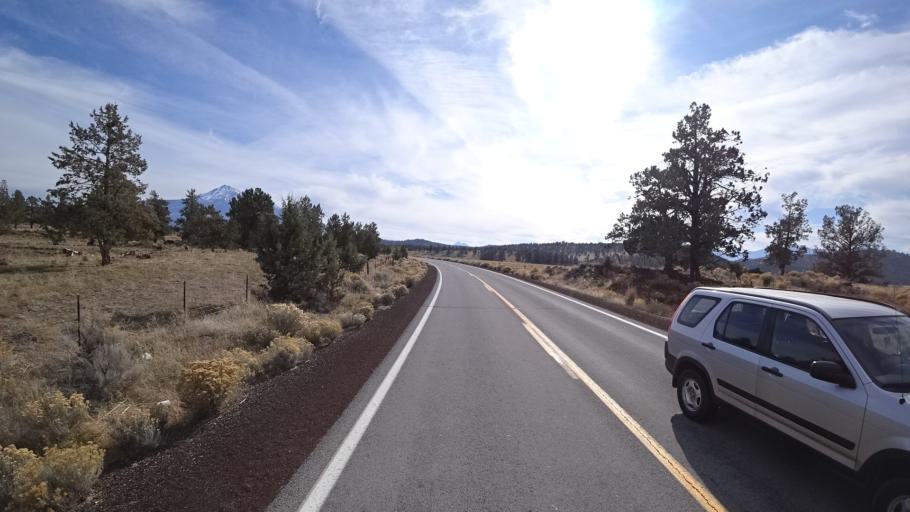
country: US
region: California
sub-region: Siskiyou County
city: Weed
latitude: 41.5583
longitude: -122.3872
